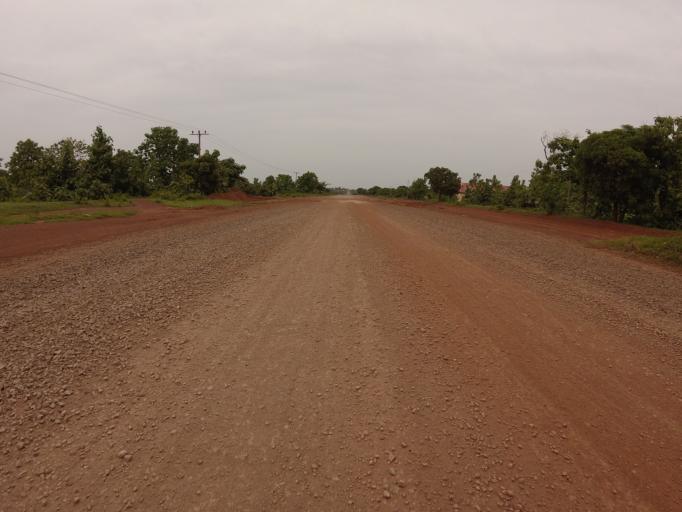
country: GH
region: Northern
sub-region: Yendi
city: Yendi
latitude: 9.2061
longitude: 0.0212
